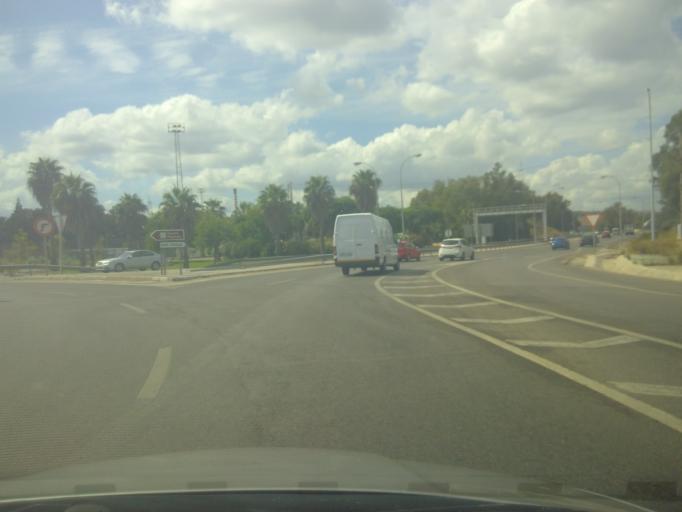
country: ES
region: Andalusia
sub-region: Provincia de Cadiz
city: San Roque
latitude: 36.1826
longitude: -5.3808
